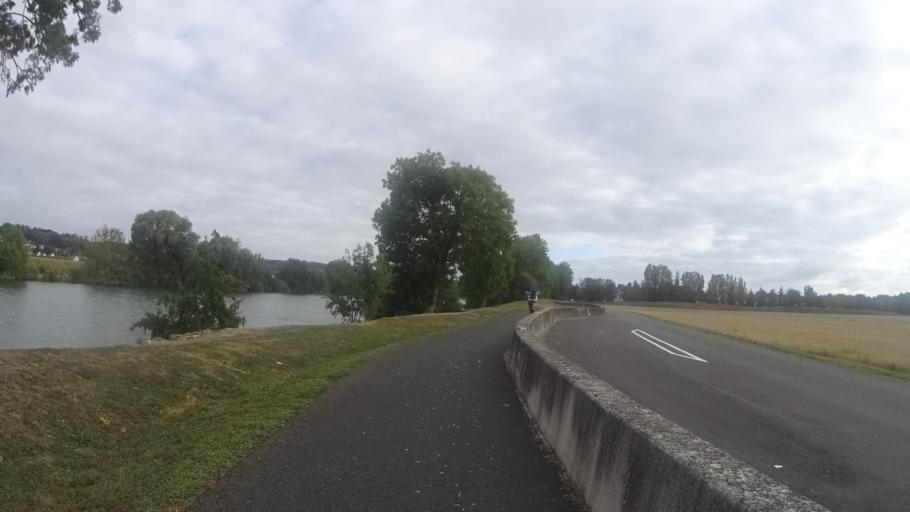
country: FR
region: Picardie
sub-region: Departement de l'Oise
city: Lacroix-Saint-Ouen
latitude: 49.3658
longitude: 2.7694
